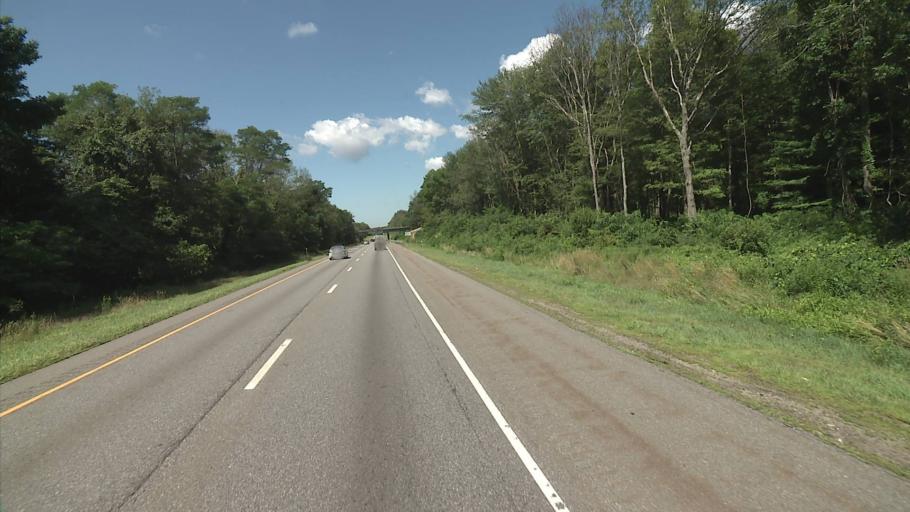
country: US
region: Connecticut
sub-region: New London County
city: Old Mystic
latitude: 41.3757
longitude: -71.9143
